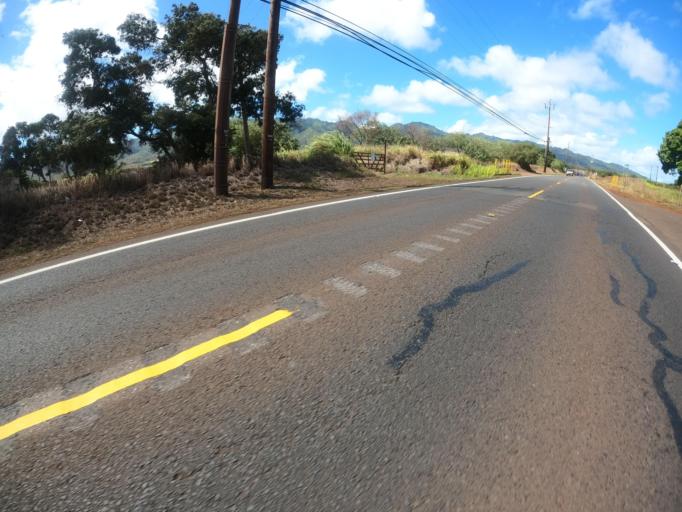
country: US
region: Hawaii
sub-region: Honolulu County
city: Village Park
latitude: 21.4192
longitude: -158.0490
